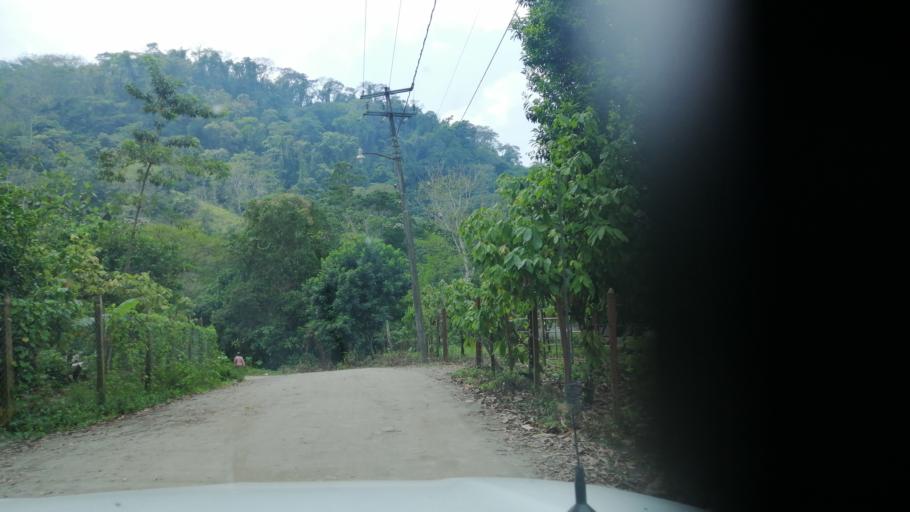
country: MX
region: Chiapas
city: Ostuacan
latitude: 17.3970
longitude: -93.3295
